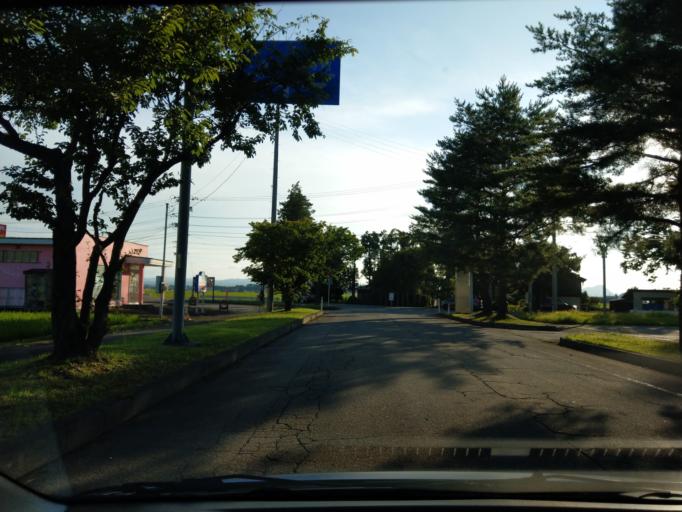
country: JP
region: Akita
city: Omagari
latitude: 39.4606
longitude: 140.5808
